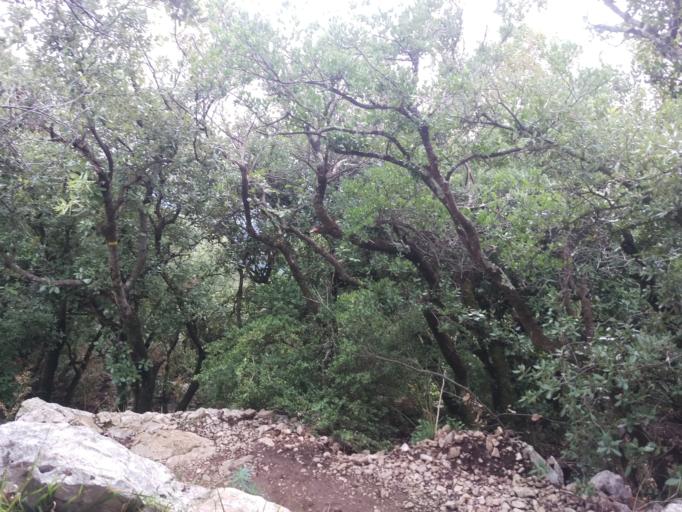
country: FR
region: Languedoc-Roussillon
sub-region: Departement de l'Herault
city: Saint-Mathieu-de-Treviers
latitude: 43.7778
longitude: 3.8127
